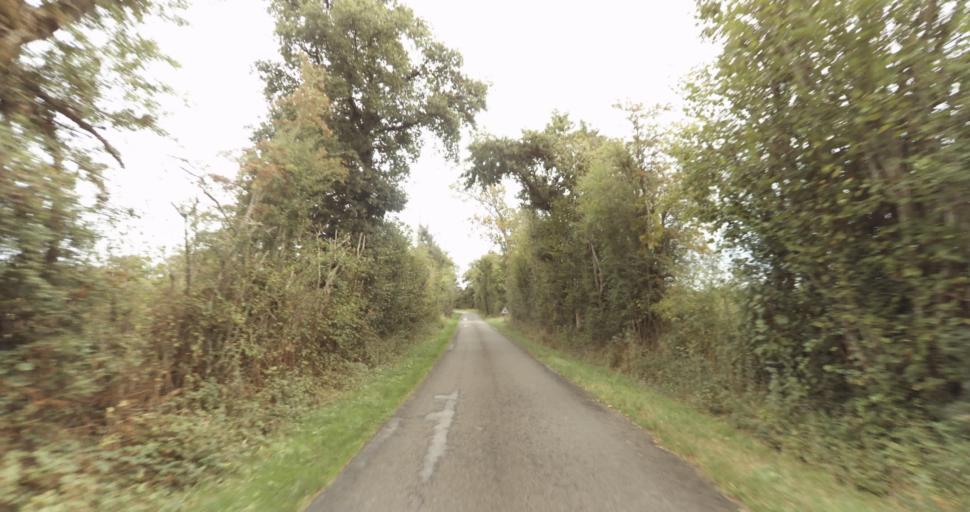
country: FR
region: Lower Normandy
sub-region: Departement de l'Orne
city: Gace
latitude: 48.7278
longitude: 0.2845
